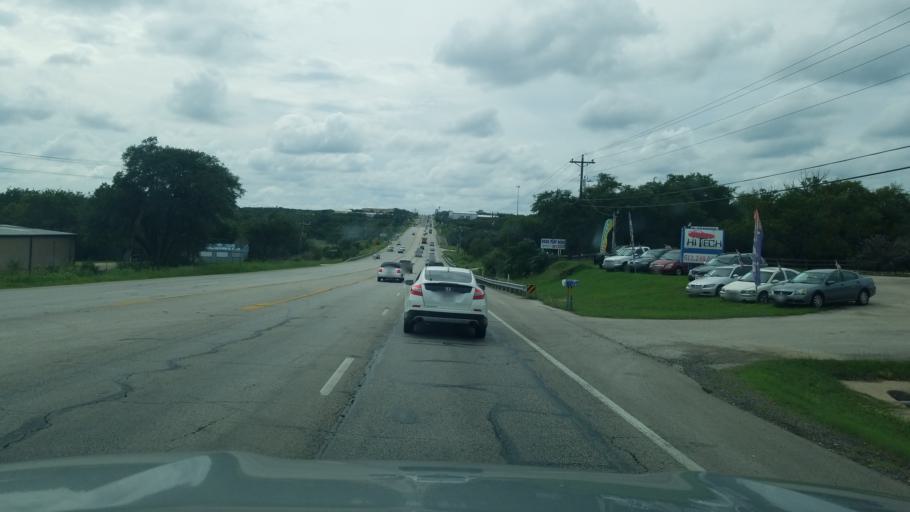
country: US
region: Texas
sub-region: Travis County
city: Barton Creek
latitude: 30.2343
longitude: -97.9193
